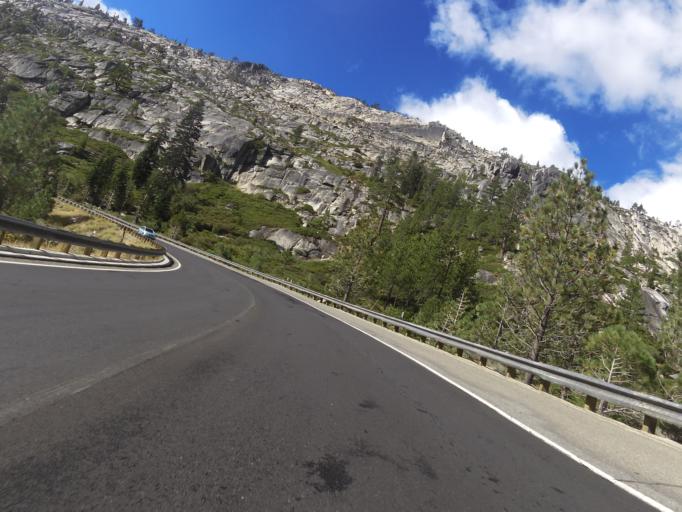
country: US
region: California
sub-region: El Dorado County
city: South Lake Tahoe
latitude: 38.8424
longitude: -120.0422
